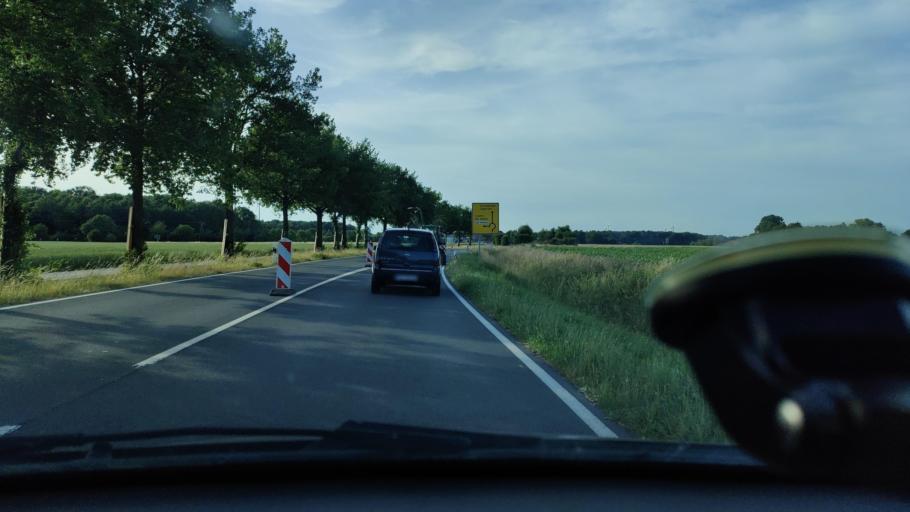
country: DE
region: North Rhine-Westphalia
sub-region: Regierungsbezirk Munster
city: Schoppingen
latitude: 52.0276
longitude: 7.2078
